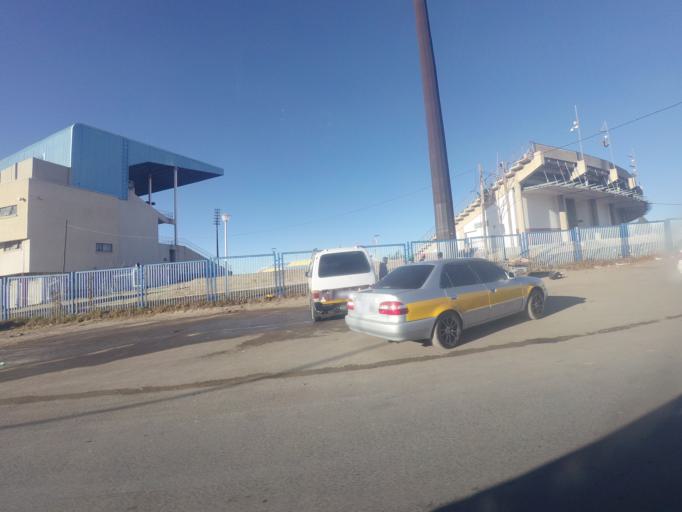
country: LS
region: Maseru
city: Maseru
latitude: -29.3117
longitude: 27.5005
